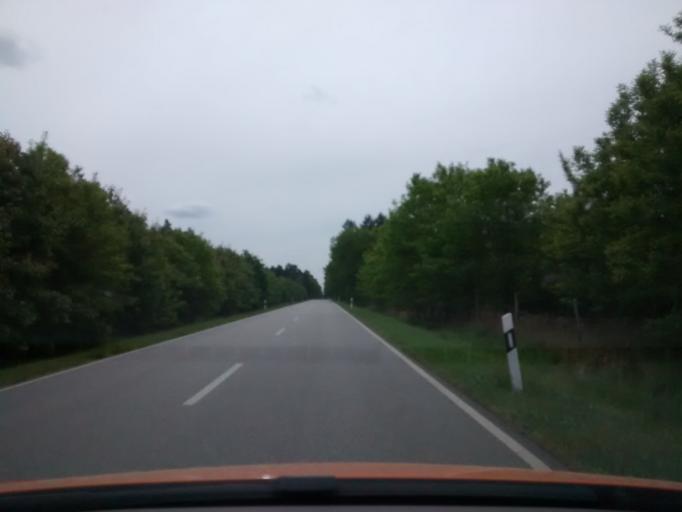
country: DE
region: Saxony-Anhalt
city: Holzdorf
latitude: 51.8797
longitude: 13.1433
